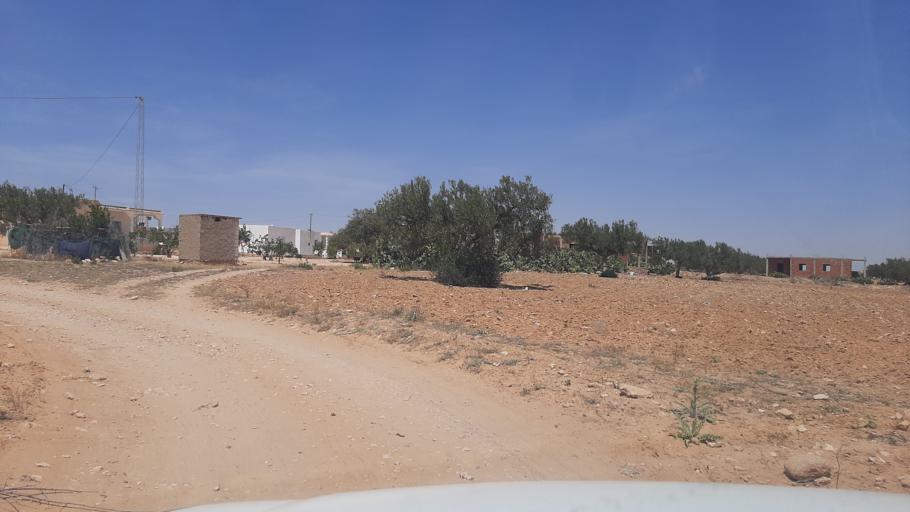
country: TN
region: Safaqis
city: Bi'r `Ali Bin Khalifah
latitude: 34.5673
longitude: 10.3473
